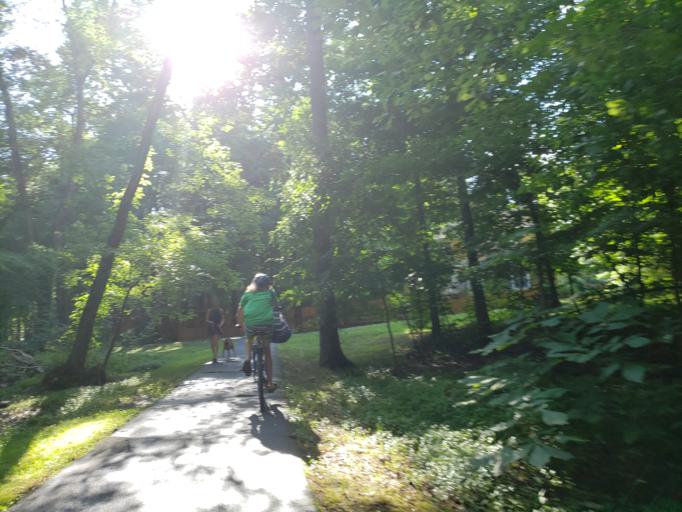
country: US
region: North Carolina
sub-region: Durham County
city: Durham
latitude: 35.9199
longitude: -78.9484
